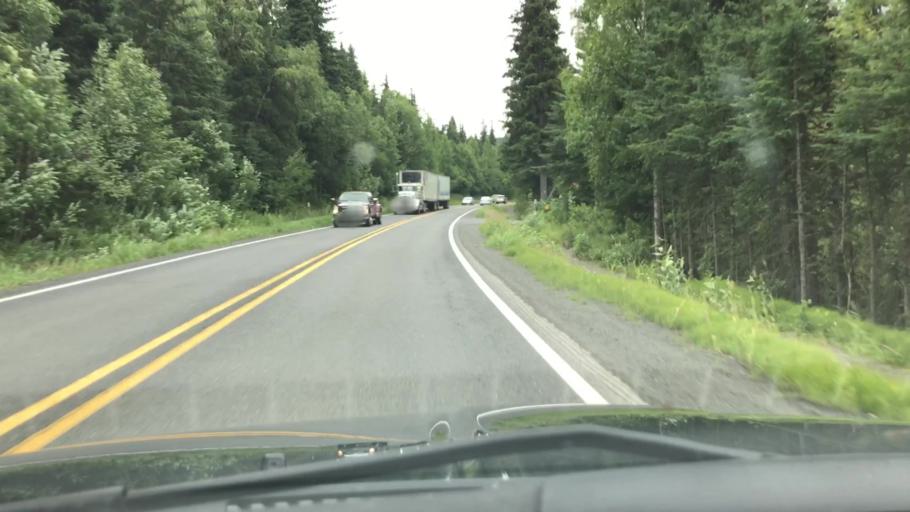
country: US
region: Alaska
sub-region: Kenai Peninsula Borough
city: Seward
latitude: 60.4861
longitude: -149.8664
